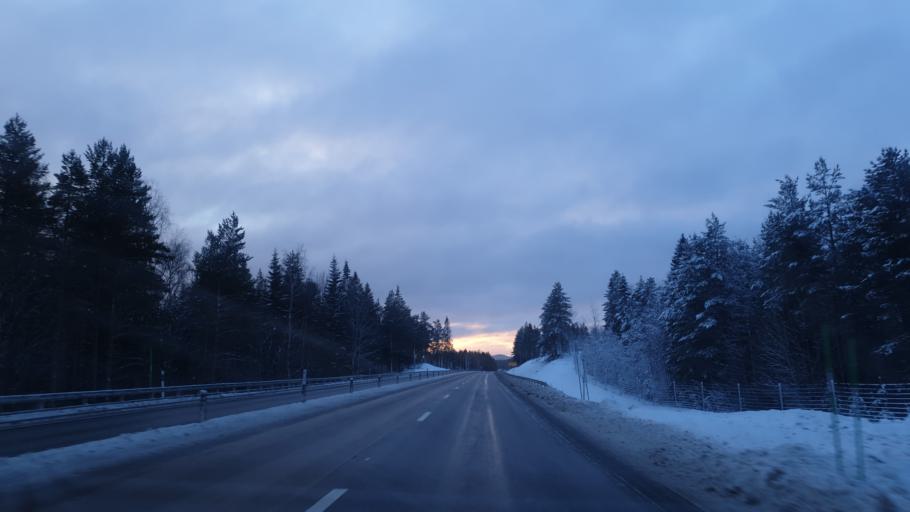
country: SE
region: Vaesterbotten
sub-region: Nordmalings Kommun
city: Nordmaling
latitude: 63.4887
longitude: 19.3108
